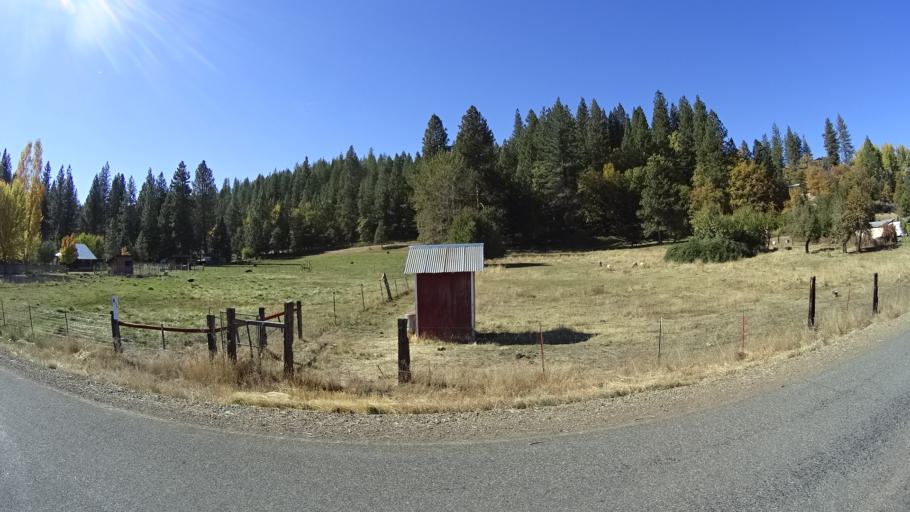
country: US
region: California
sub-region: Siskiyou County
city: Yreka
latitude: 41.6060
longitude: -122.9768
